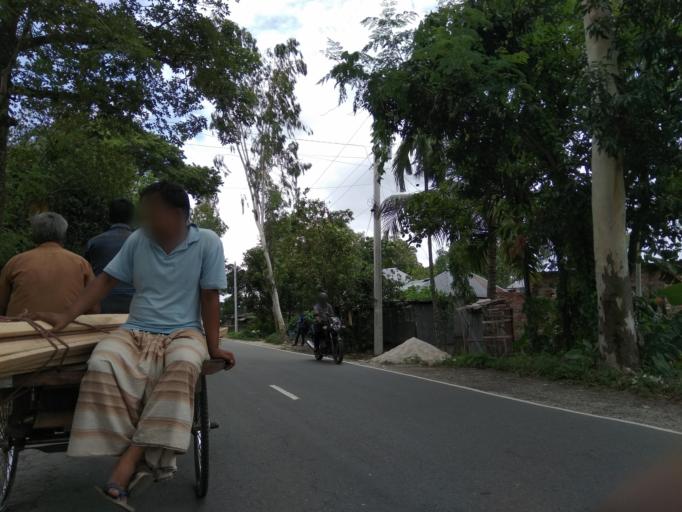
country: BD
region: Rajshahi
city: Saidpur
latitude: 25.7717
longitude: 88.8003
